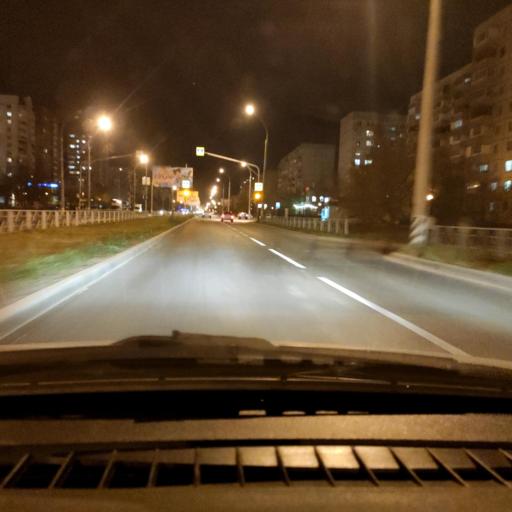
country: RU
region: Samara
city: Tol'yatti
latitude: 53.5478
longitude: 49.3320
